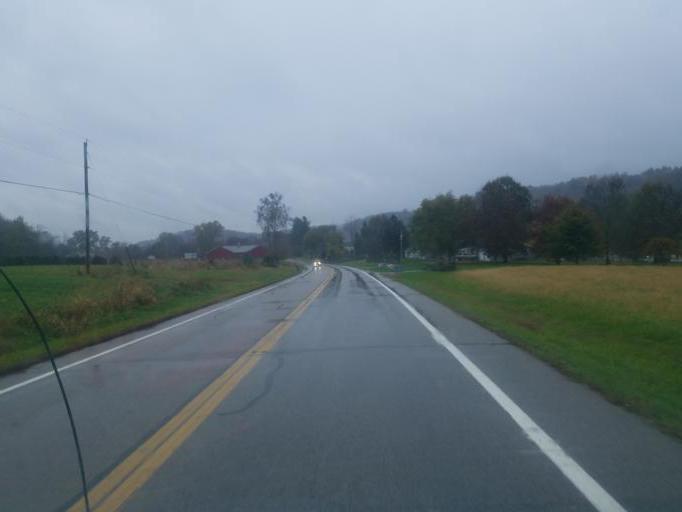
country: US
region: Ohio
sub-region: Morgan County
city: McConnelsville
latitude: 39.7387
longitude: -81.9121
